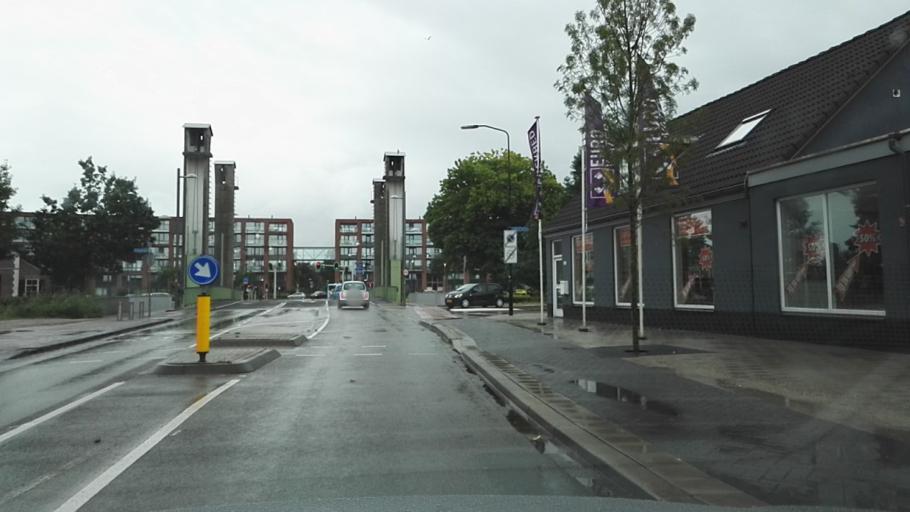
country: NL
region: Gelderland
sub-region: Gemeente Apeldoorn
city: Apeldoorn
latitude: 52.2119
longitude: 5.9746
